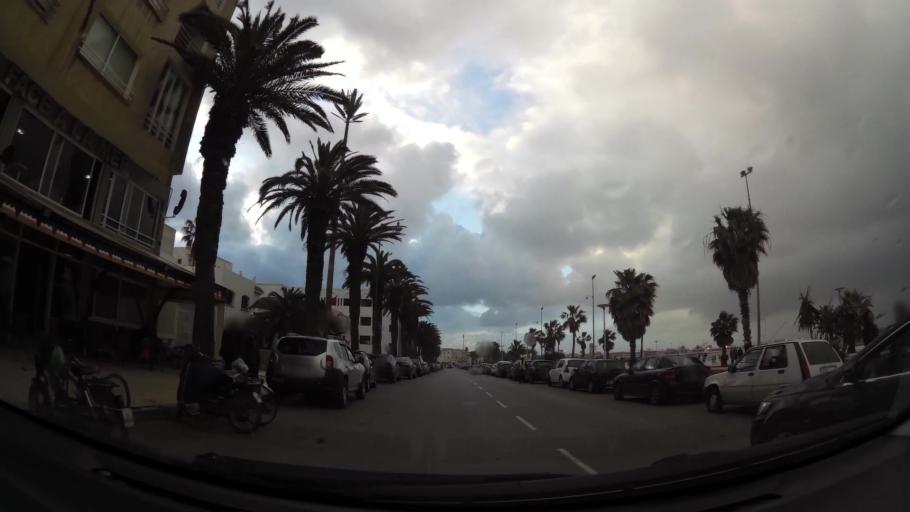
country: MA
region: Doukkala-Abda
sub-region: El-Jadida
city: El Jadida
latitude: 33.2499
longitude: -8.4987
